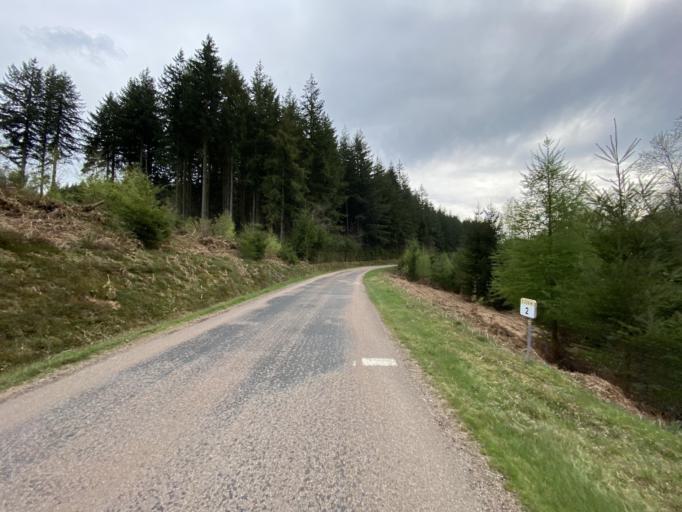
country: FR
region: Bourgogne
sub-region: Departement de la Cote-d'Or
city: Saulieu
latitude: 47.3149
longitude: 4.0937
